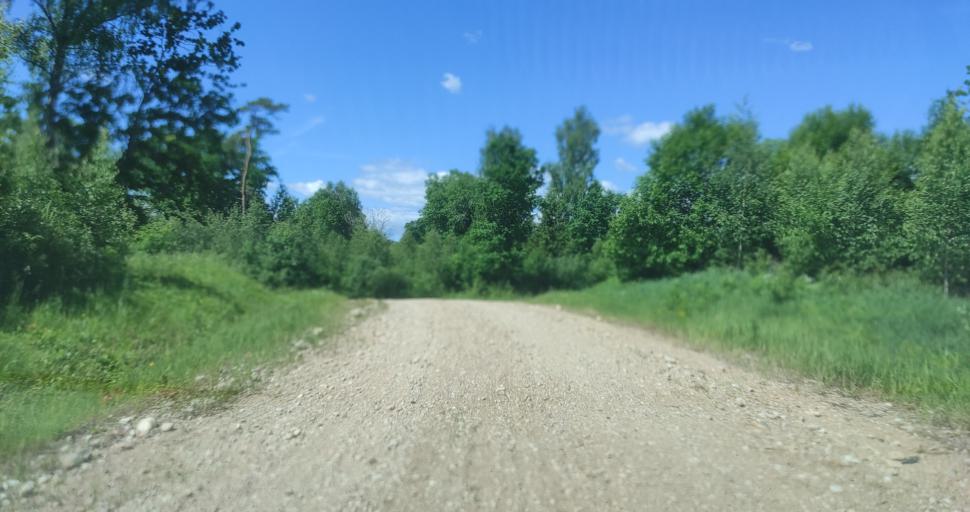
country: LV
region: Alsunga
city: Alsunga
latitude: 56.8867
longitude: 21.7234
